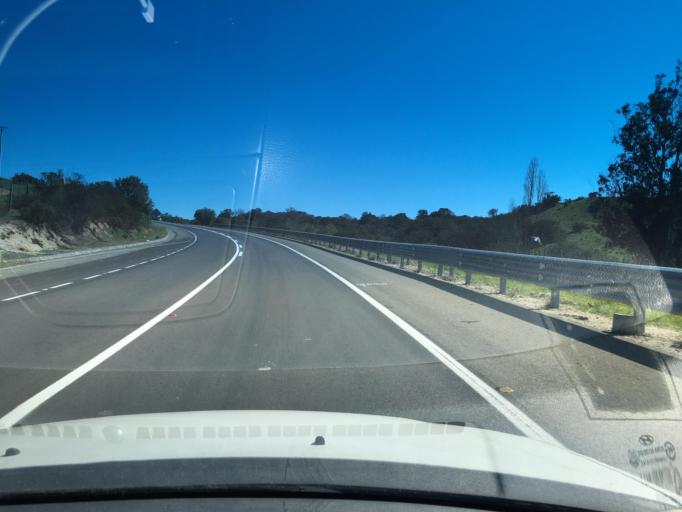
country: CL
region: Valparaiso
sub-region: San Antonio Province
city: El Tabo
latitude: -33.4052
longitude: -71.5253
